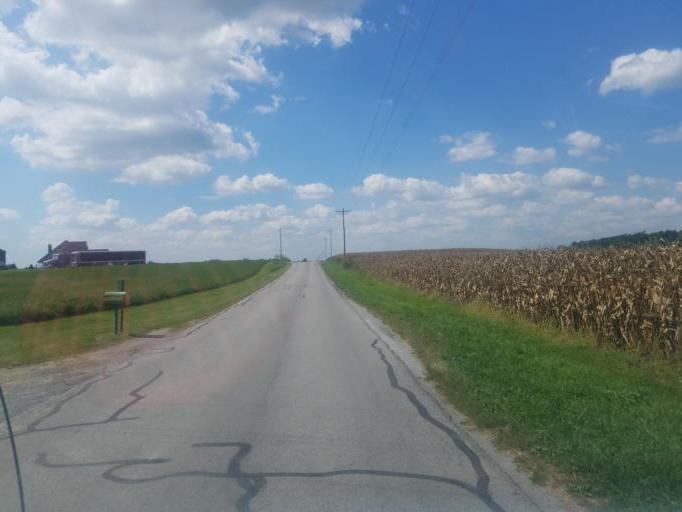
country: US
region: Ohio
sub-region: Hardin County
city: Ada
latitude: 40.6519
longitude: -83.9195
